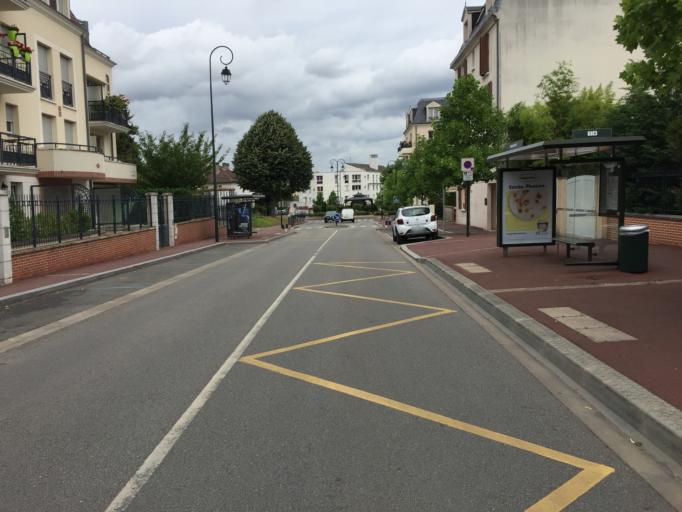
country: FR
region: Ile-de-France
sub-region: Departement des Yvelines
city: Les Clayes-sous-Bois
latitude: 48.8209
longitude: 1.9888
